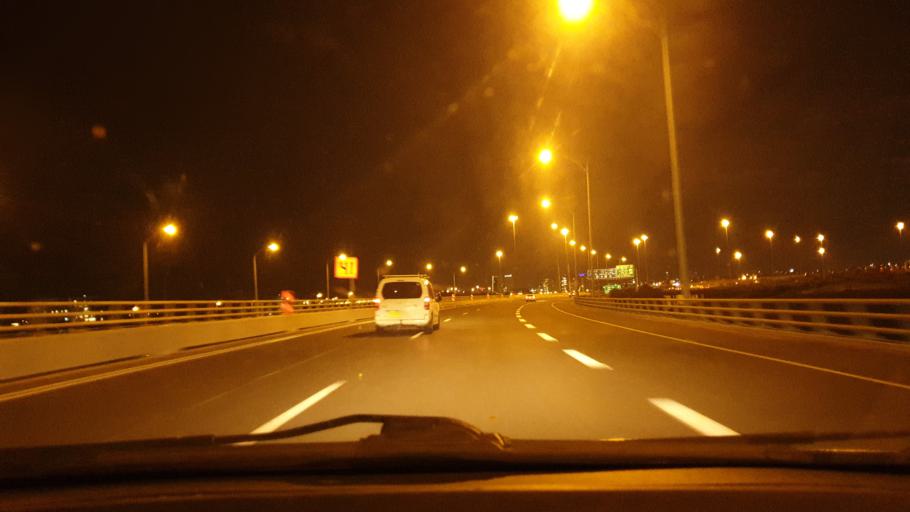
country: IL
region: Central District
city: Ness Ziona
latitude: 31.9329
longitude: 34.8173
